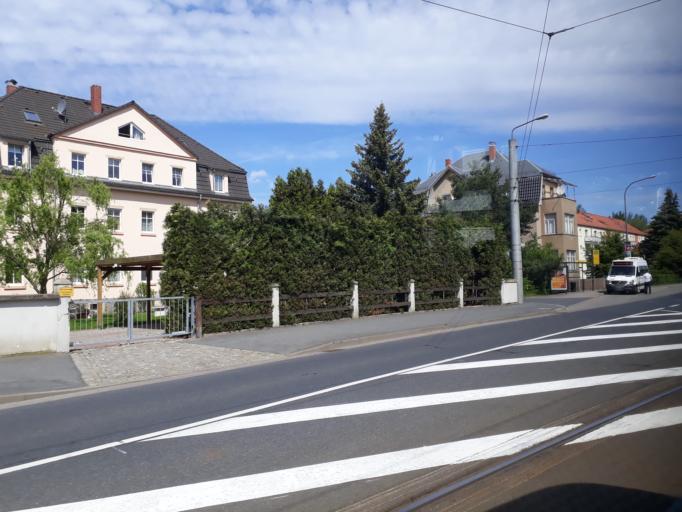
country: DE
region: Saxony
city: Albertstadt
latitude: 51.1219
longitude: 13.7911
